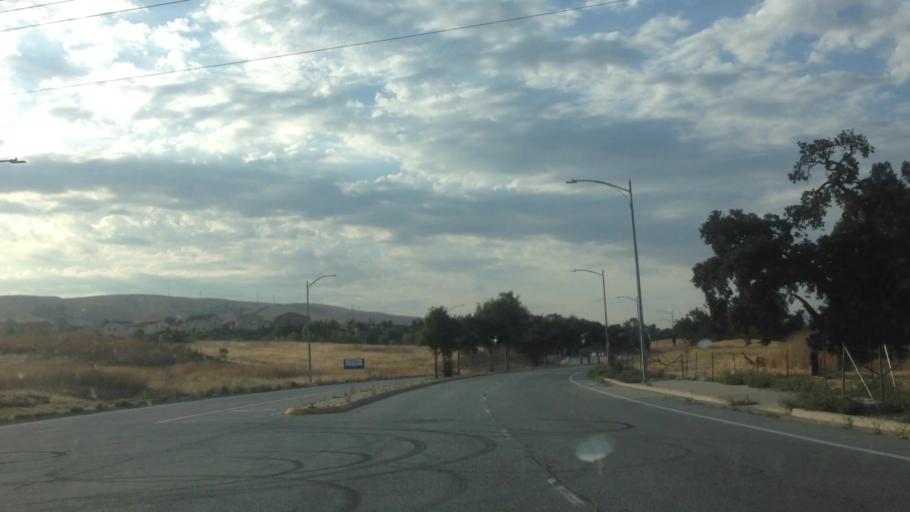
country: US
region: California
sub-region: Santa Clara County
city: Seven Trees
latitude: 37.2523
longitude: -121.7736
